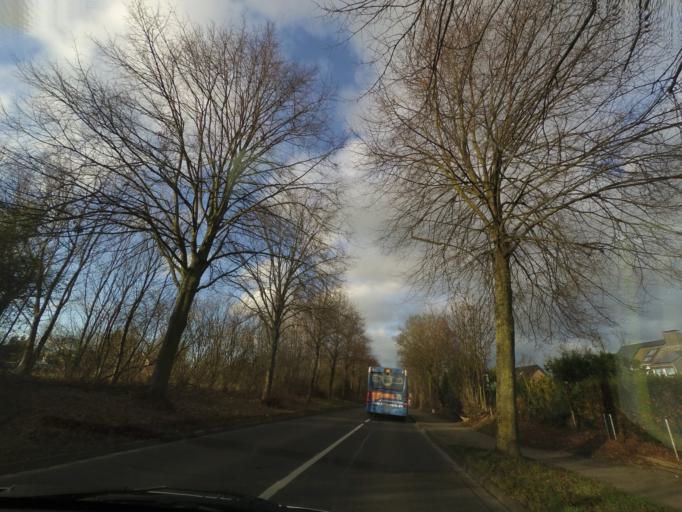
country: DE
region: North Rhine-Westphalia
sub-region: Regierungsbezirk Dusseldorf
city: Grevenbroich
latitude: 51.1155
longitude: 6.5653
